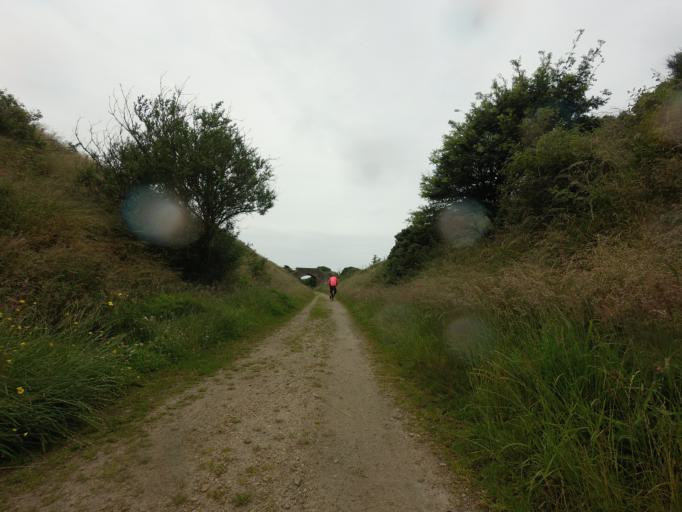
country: GB
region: Scotland
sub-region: Moray
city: Portknockie
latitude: 57.6990
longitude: -2.8512
